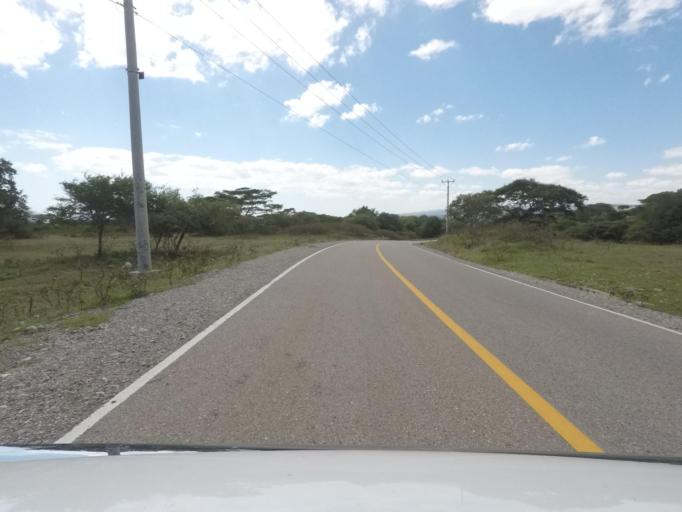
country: TL
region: Lautem
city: Lospalos
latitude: -8.4041
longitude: 126.8203
